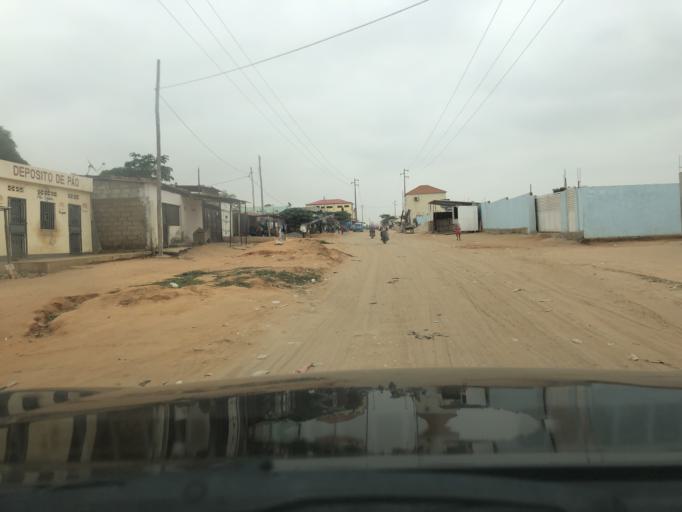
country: AO
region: Luanda
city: Luanda
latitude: -8.9381
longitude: 13.2394
